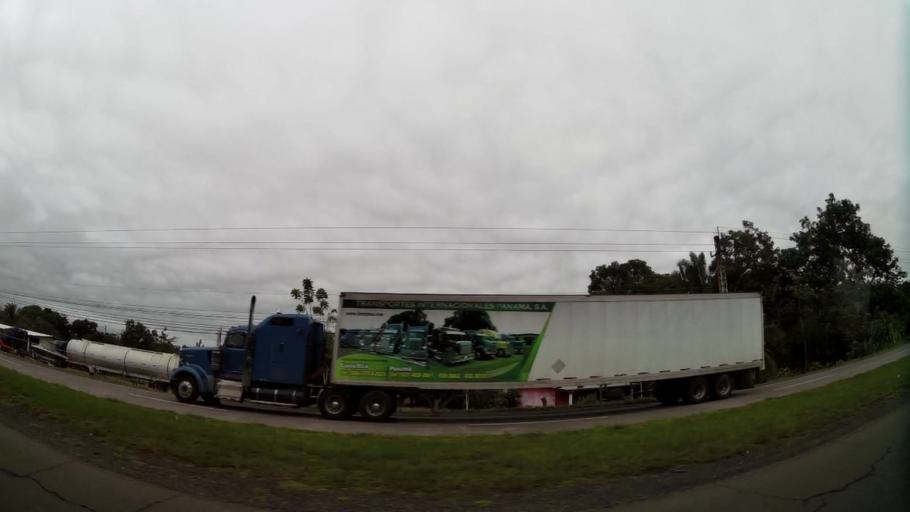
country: PA
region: Chiriqui
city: Boqueron
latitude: 8.4886
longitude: -82.5731
